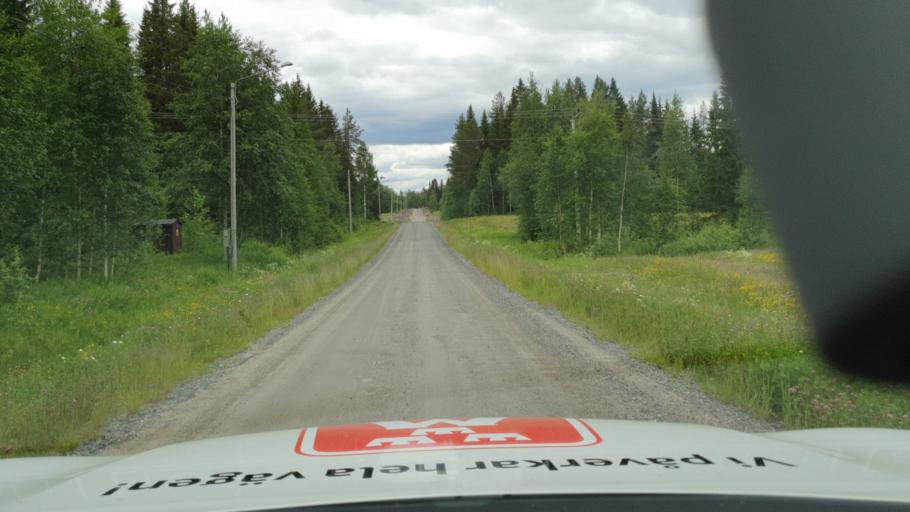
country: SE
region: Vaesterbotten
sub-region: Bjurholms Kommun
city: Bjurholm
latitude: 63.7440
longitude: 19.2771
